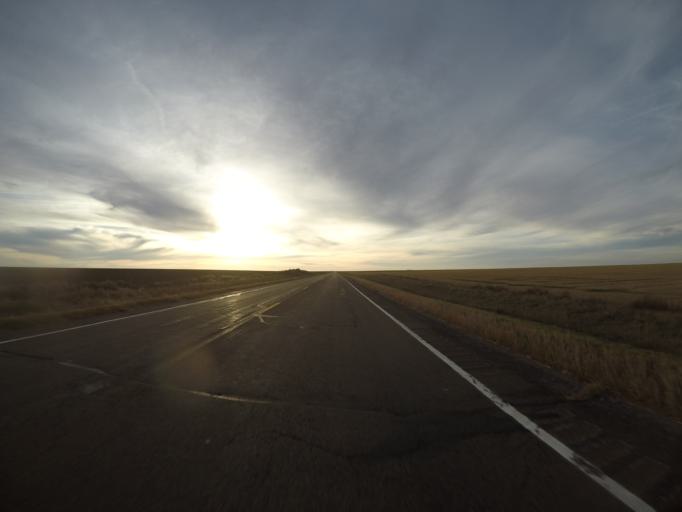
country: US
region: Colorado
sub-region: Washington County
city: Akron
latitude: 39.7274
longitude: -103.1323
